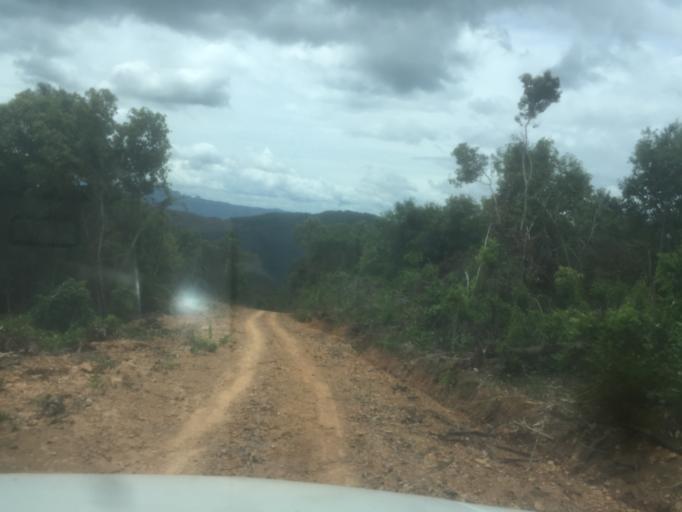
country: LA
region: Phongsali
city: Khoa
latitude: 20.9240
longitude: 102.5531
